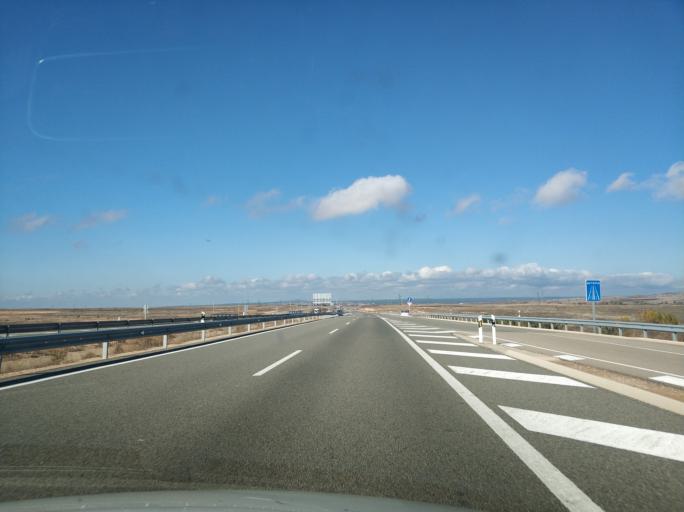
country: ES
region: Castille and Leon
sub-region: Provincia de Soria
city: Coscurita
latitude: 41.4215
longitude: -2.4899
